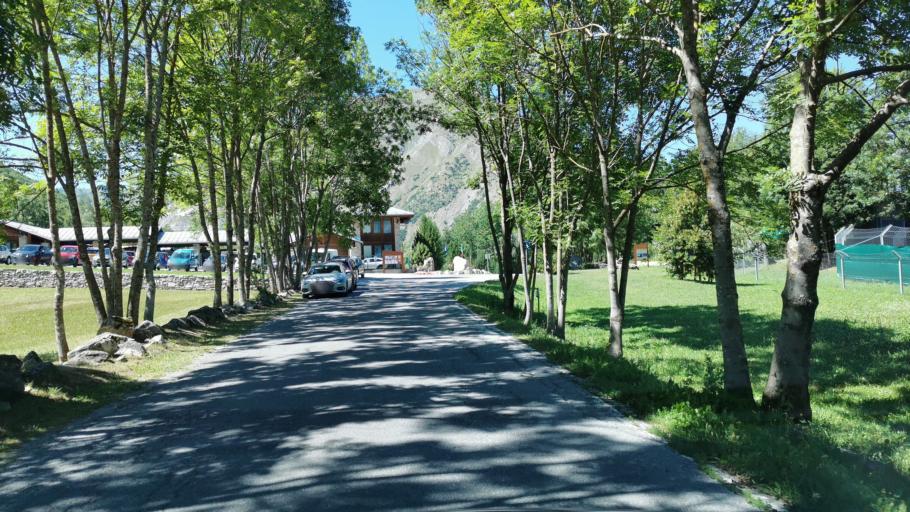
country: IT
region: Piedmont
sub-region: Provincia di Cuneo
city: Entracque
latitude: 44.2496
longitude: 7.3848
